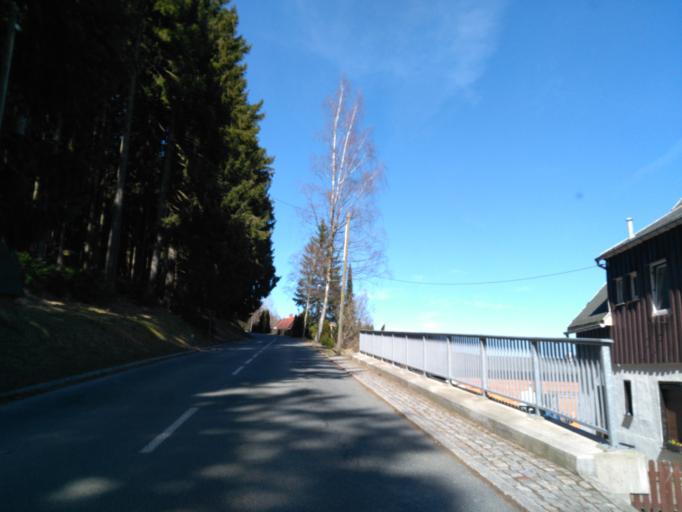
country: DE
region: Saxony
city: Rittersgrun
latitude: 50.4701
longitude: 12.8040
